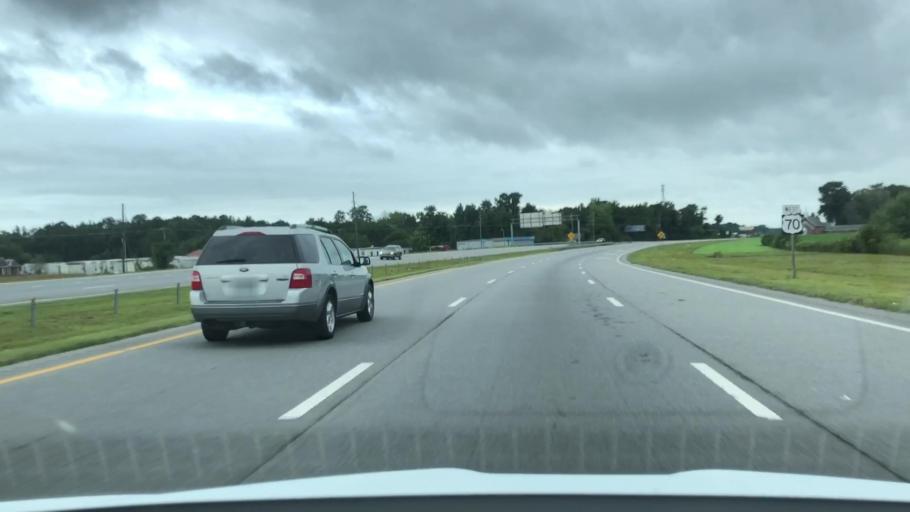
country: US
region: North Carolina
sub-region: Lenoir County
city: Kinston
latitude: 35.2629
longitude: -77.6865
